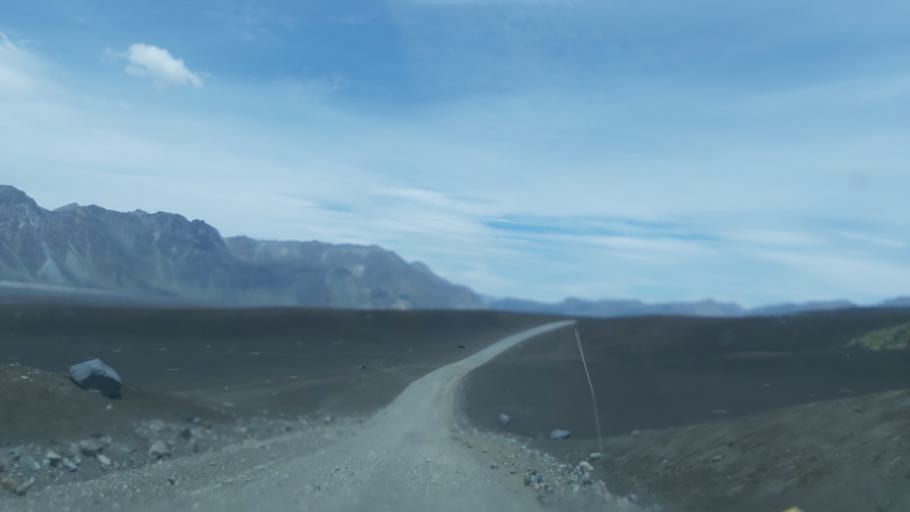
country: AR
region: Neuquen
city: Andacollo
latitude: -37.4166
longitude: -71.2896
